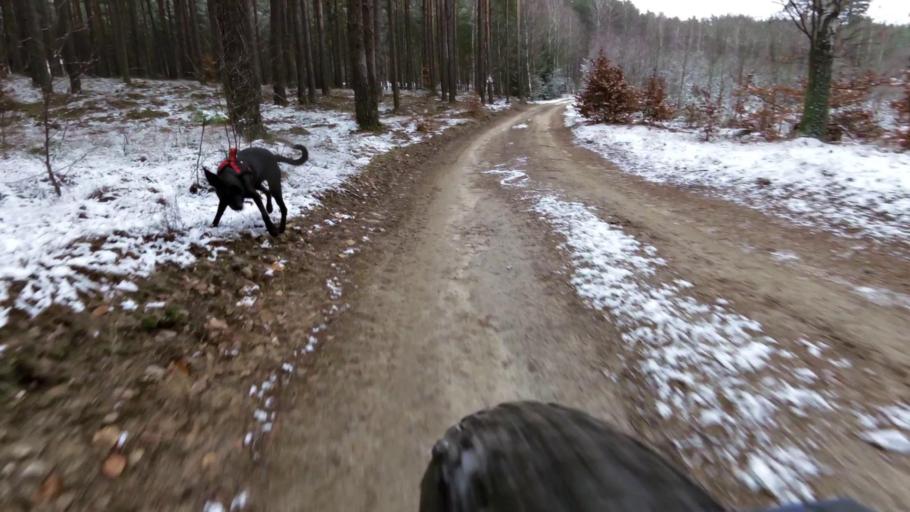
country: PL
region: West Pomeranian Voivodeship
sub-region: Powiat walecki
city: Miroslawiec
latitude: 53.3268
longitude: 16.1026
